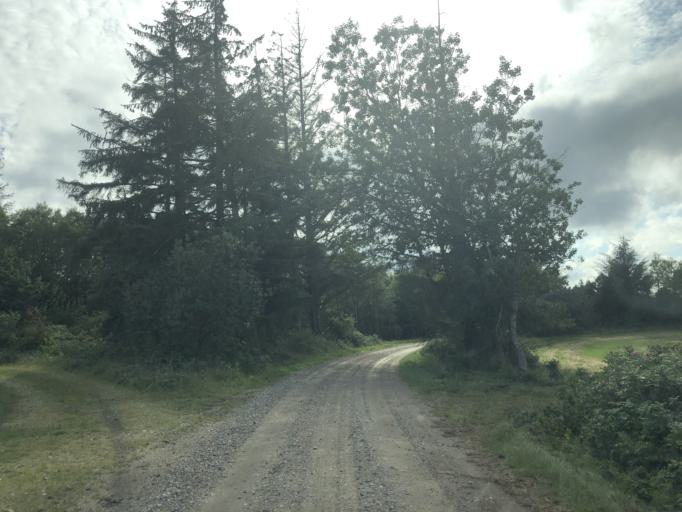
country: DK
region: Central Jutland
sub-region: Holstebro Kommune
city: Ulfborg
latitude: 56.2349
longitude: 8.4464
